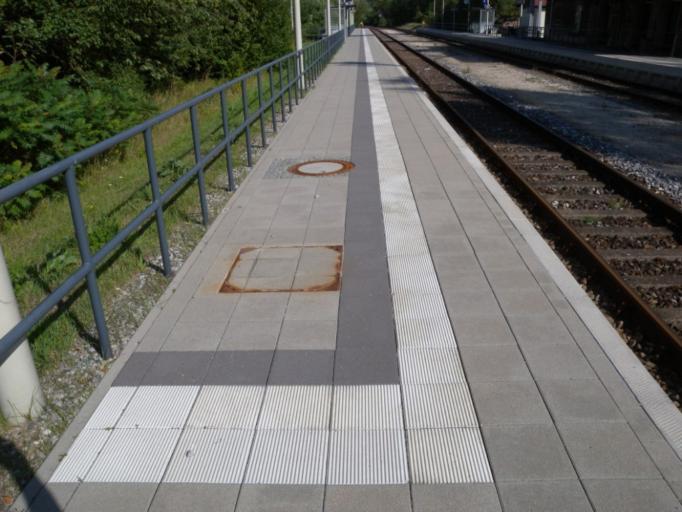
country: DE
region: Baden-Wuerttemberg
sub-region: Regierungsbezirk Stuttgart
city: Herbrechtingen
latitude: 48.6260
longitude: 10.1696
